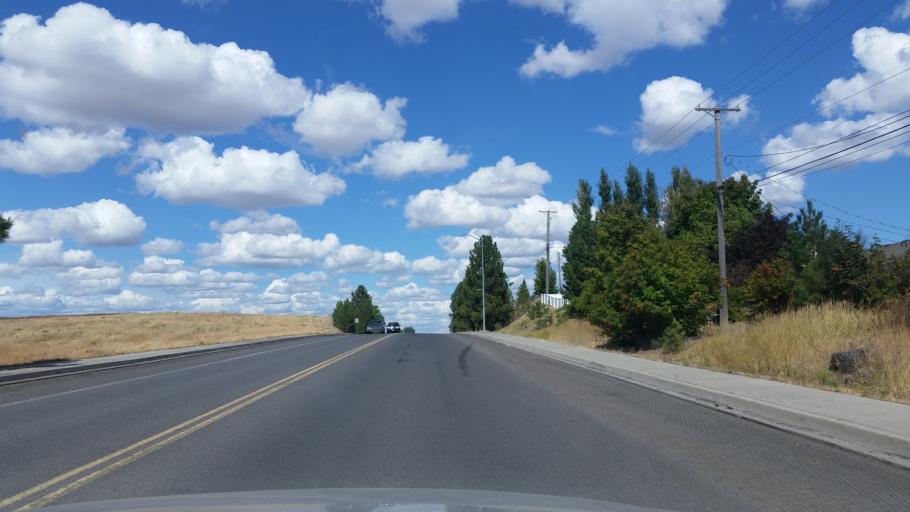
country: US
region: Washington
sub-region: Spokane County
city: Cheney
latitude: 47.4981
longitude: -117.5865
